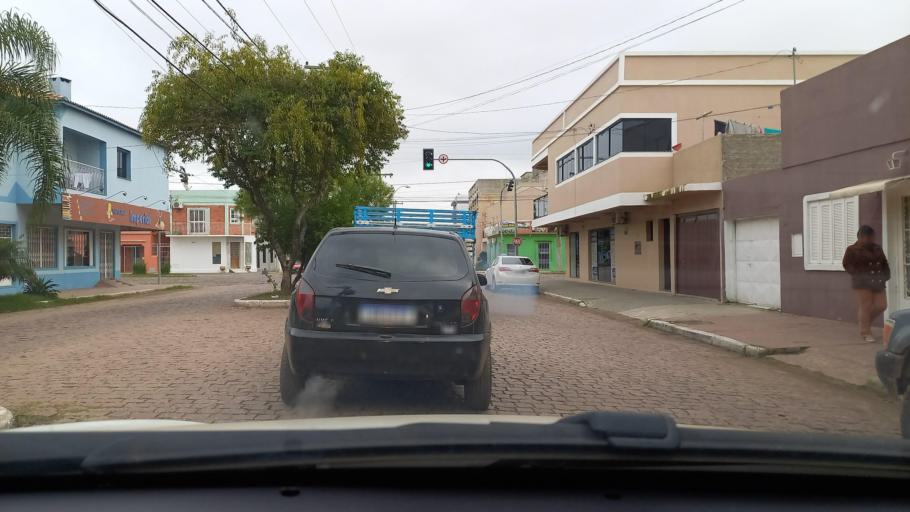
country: BR
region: Rio Grande do Sul
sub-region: Dom Pedrito
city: Dom Pedrito
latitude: -30.9795
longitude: -54.6709
